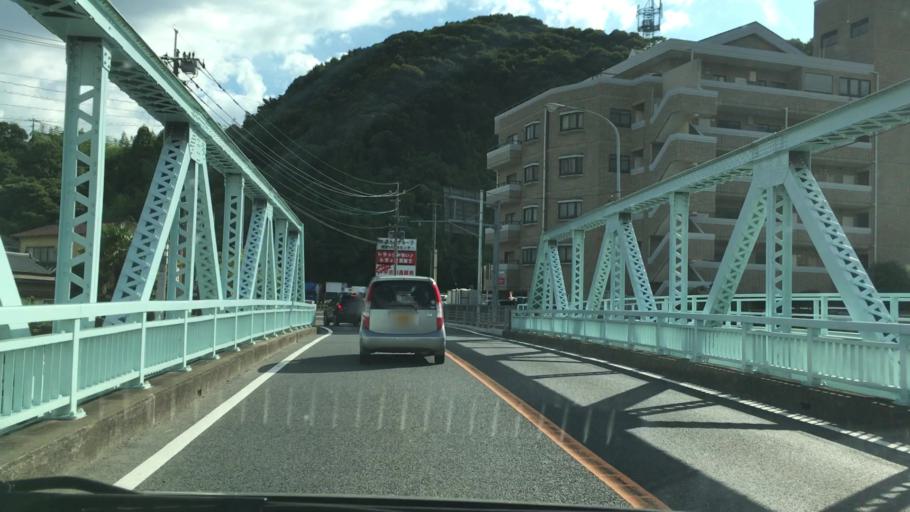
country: JP
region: Nagasaki
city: Sasebo
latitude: 33.1378
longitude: 129.7942
